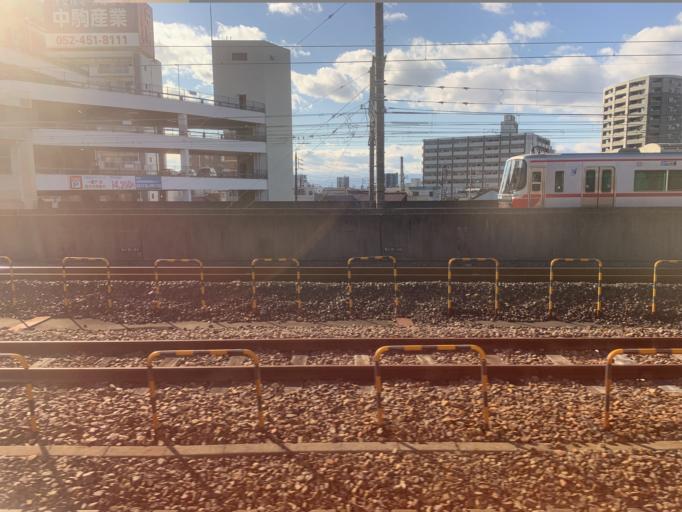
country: JP
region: Aichi
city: Ichinomiya
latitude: 35.3041
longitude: 136.7963
